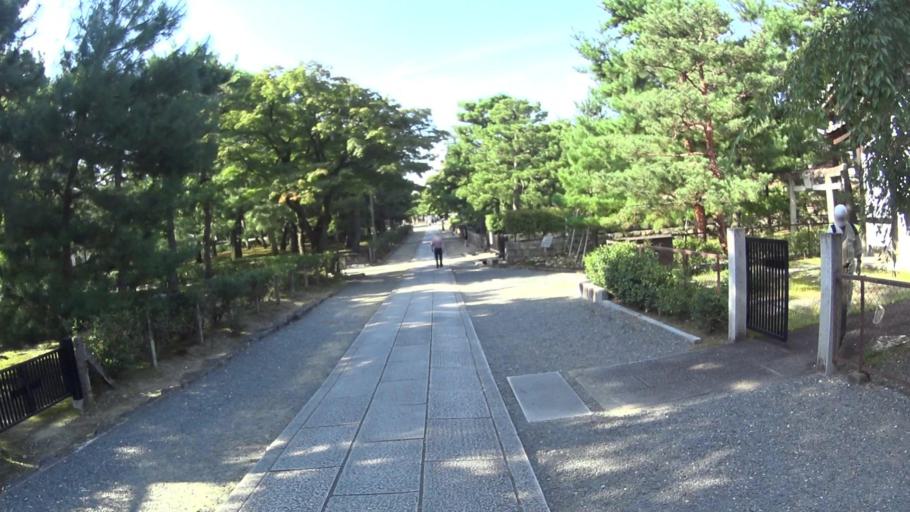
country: RU
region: Rostov
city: Remontnoye
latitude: 46.5016
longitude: 43.7566
